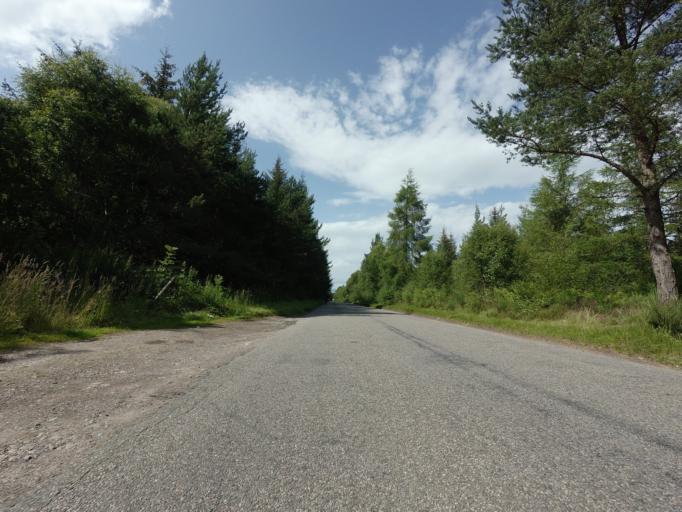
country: GB
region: Scotland
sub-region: Highland
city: Fortrose
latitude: 57.4818
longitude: -4.0904
